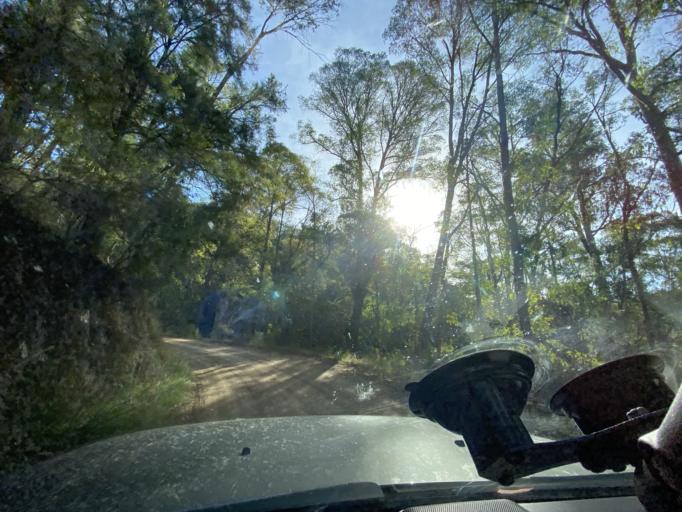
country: AU
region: Victoria
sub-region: Mansfield
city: Mansfield
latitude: -37.5178
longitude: 146.0924
